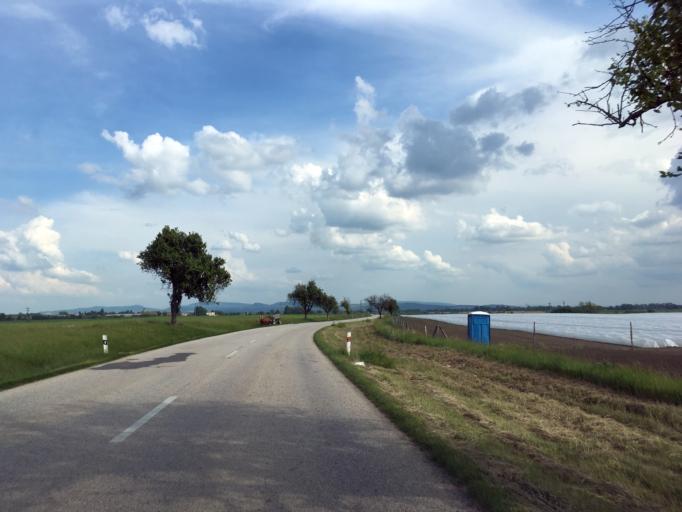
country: HU
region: Komarom-Esztergom
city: Almasfuzito
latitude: 47.7954
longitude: 18.2510
